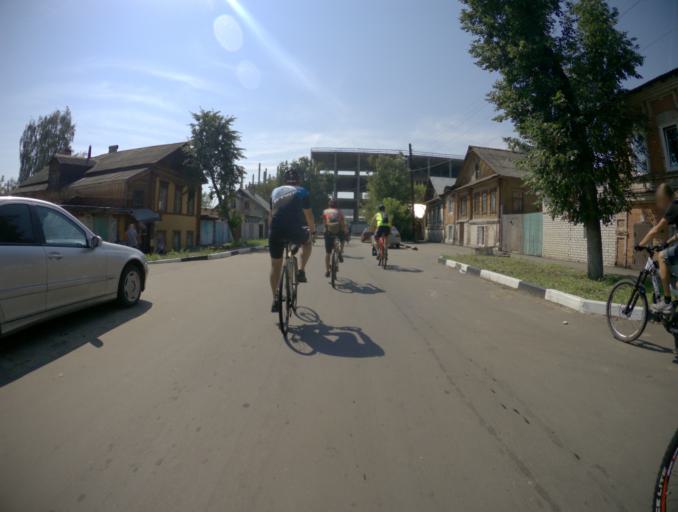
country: RU
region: Nizjnij Novgorod
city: Nizhniy Novgorod
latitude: 56.3172
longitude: 43.9491
